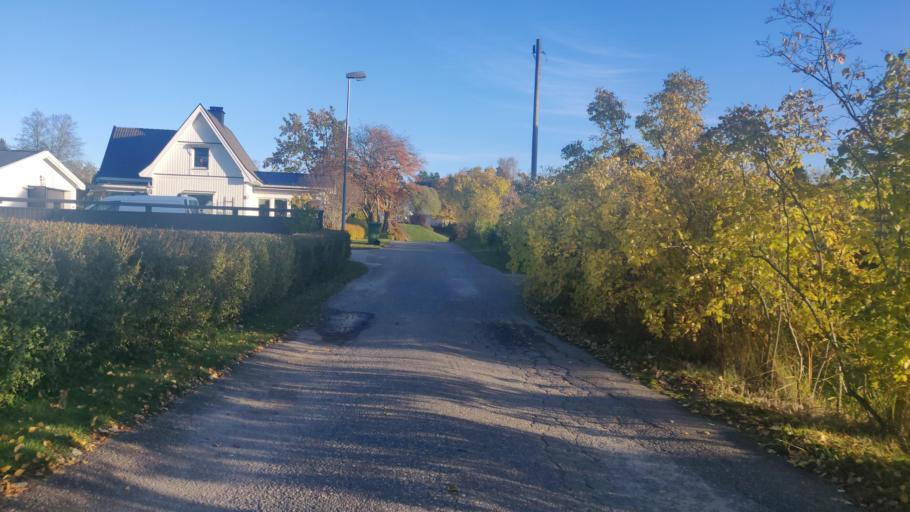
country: SE
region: Vaesternorrland
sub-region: Sundsvalls Kommun
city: Skottsund
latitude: 62.2897
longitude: 17.3835
